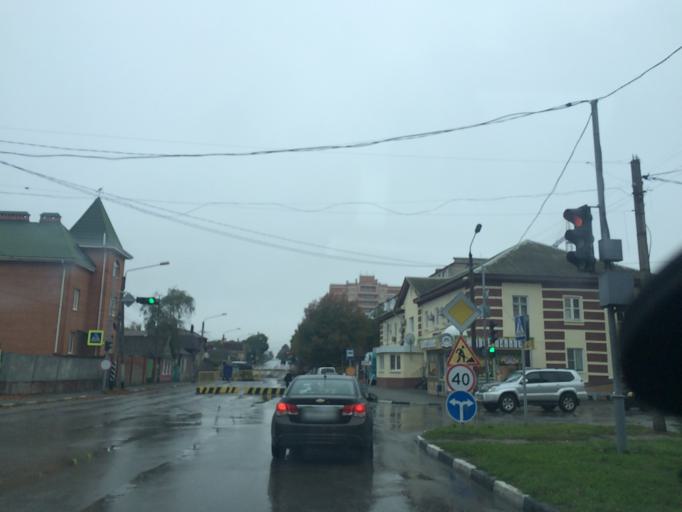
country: RU
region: Rostov
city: Azov
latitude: 47.1062
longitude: 39.4315
